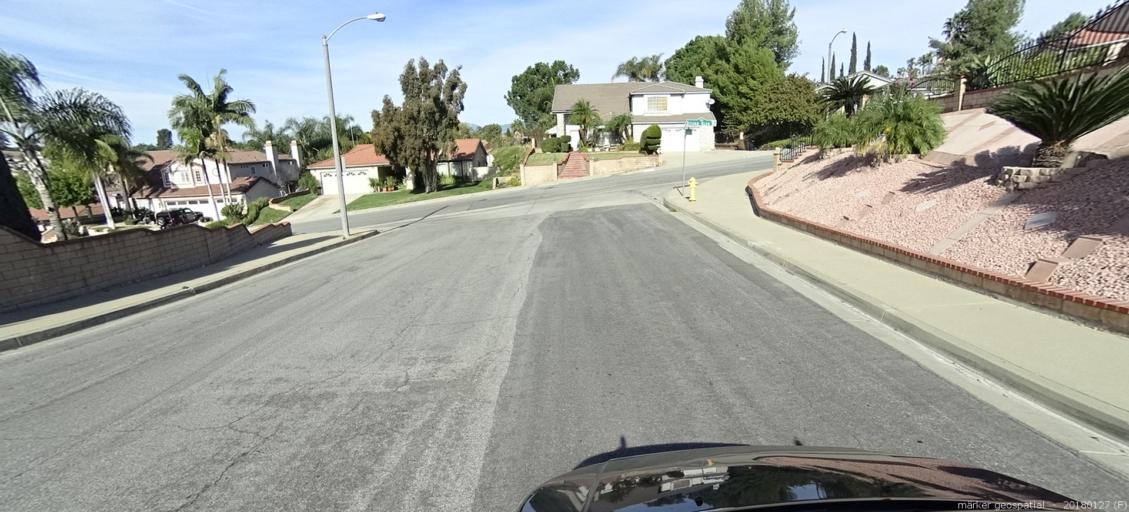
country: US
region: California
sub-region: Los Angeles County
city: Diamond Bar
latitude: 34.0320
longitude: -117.7885
